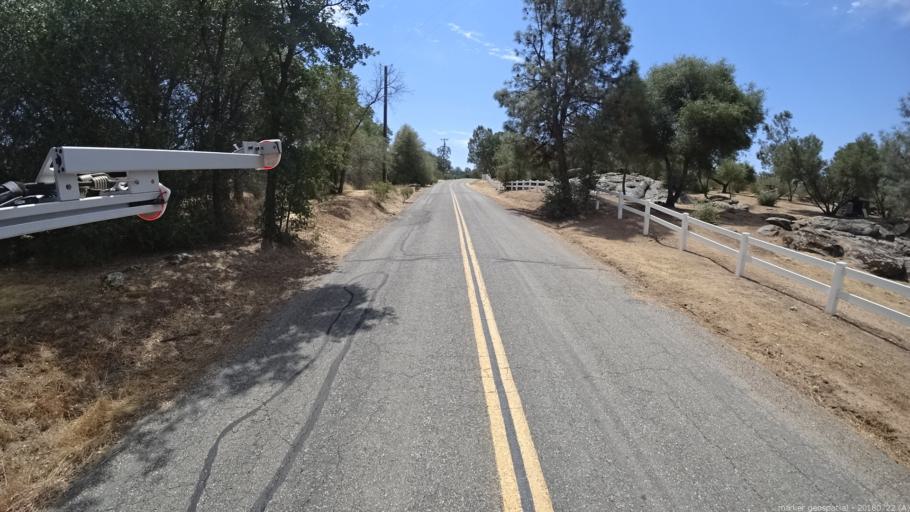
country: US
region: California
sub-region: Madera County
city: Coarsegold
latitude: 37.2840
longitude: -119.7457
